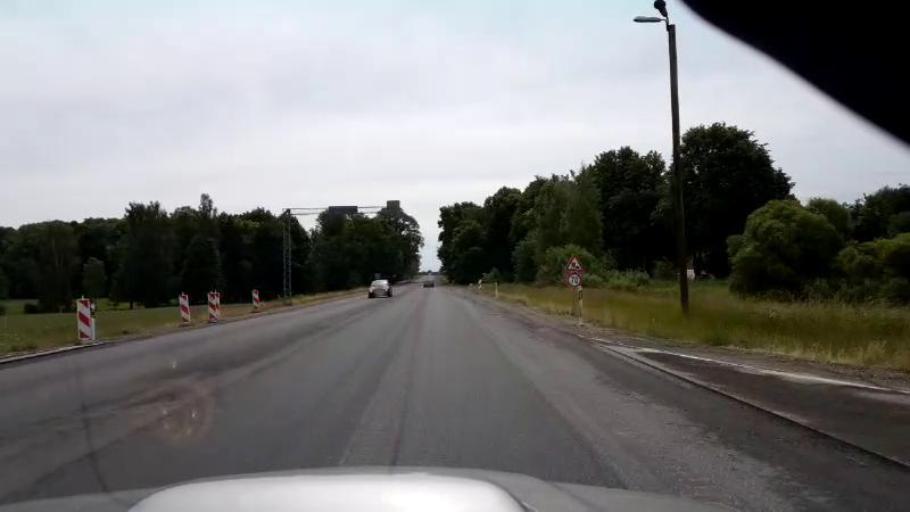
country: LV
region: Bauskas Rajons
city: Bauska
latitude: 56.3796
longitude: 24.2620
